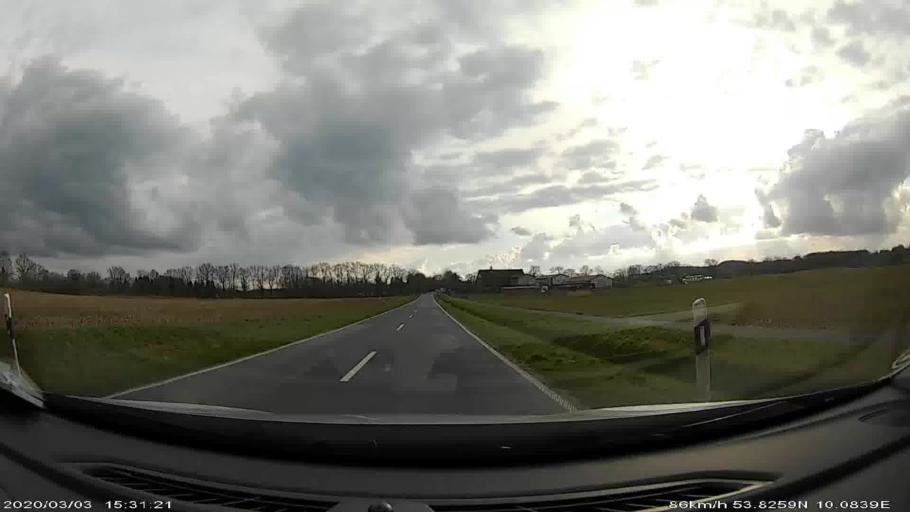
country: DE
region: Schleswig-Holstein
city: Huttblek
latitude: 53.8271
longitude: 10.0843
